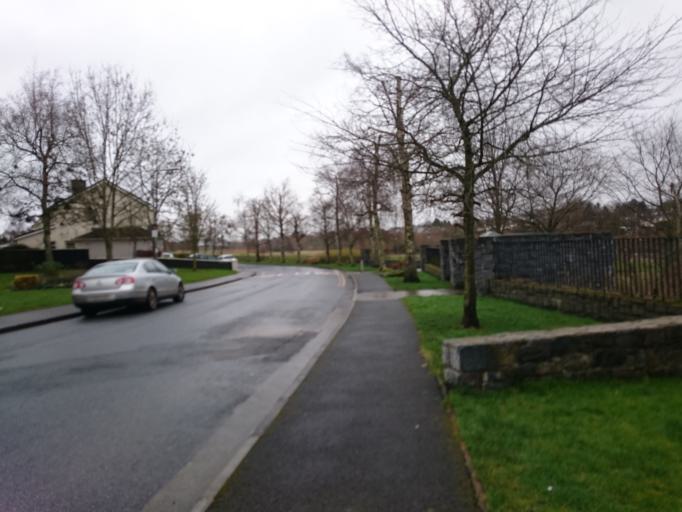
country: IE
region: Leinster
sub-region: Kilkenny
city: Kilkenny
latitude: 52.6599
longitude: -7.2567
